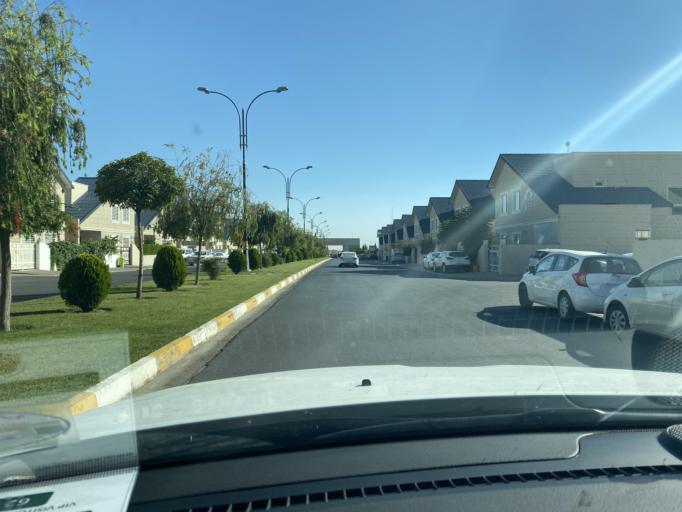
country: IQ
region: Arbil
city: Erbil
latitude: 36.2408
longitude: 44.0505
